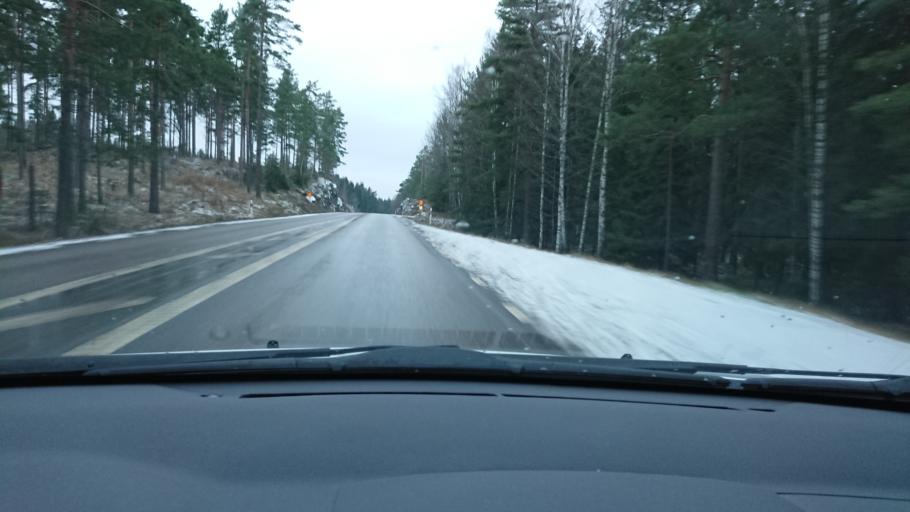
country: SE
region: Kalmar
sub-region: Hultsfreds Kommun
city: Hultsfred
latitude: 57.4902
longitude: 15.8252
